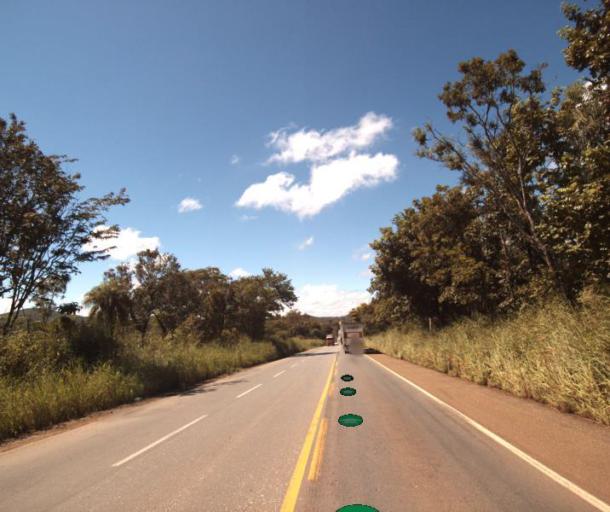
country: BR
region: Goias
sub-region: Jaragua
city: Jaragua
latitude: -15.6688
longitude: -49.3504
